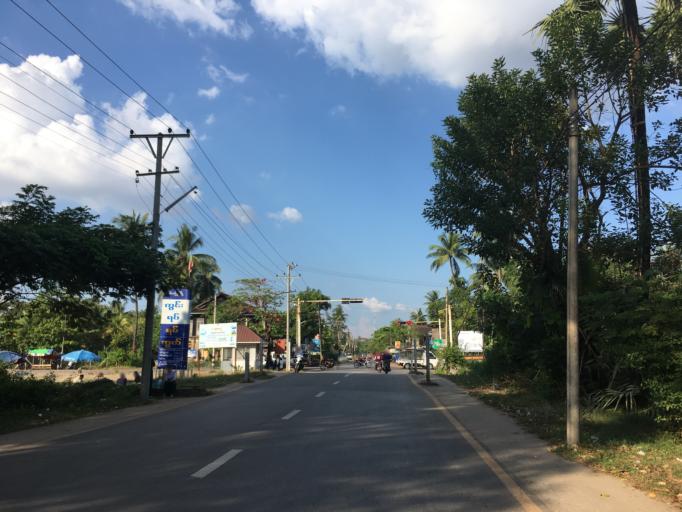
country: MM
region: Mon
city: Mawlamyine
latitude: 16.4505
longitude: 97.6243
